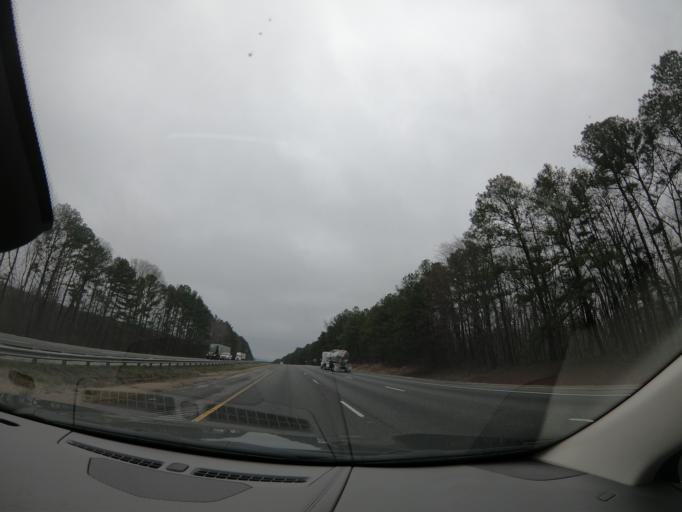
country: US
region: Georgia
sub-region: Gordon County
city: Calhoun
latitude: 34.6159
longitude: -84.9642
